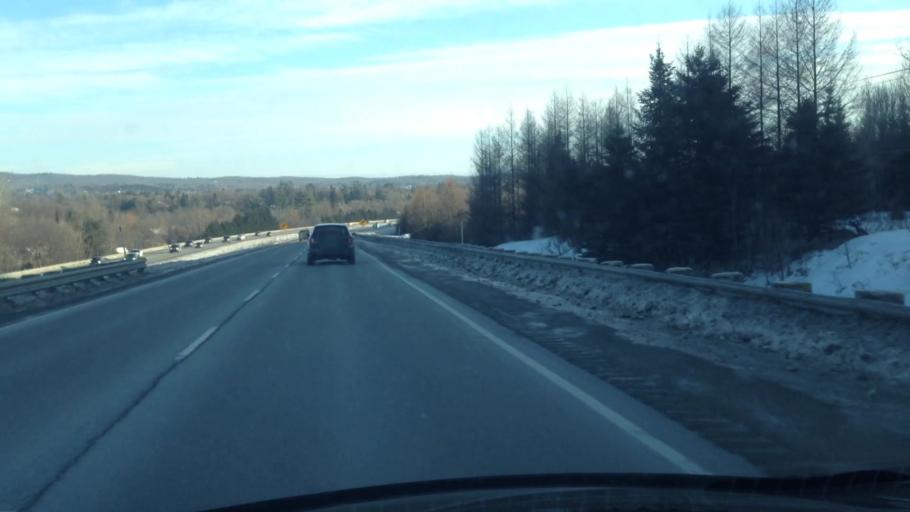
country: CA
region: Quebec
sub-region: Laurentides
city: Prevost
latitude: 45.8775
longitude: -74.0938
